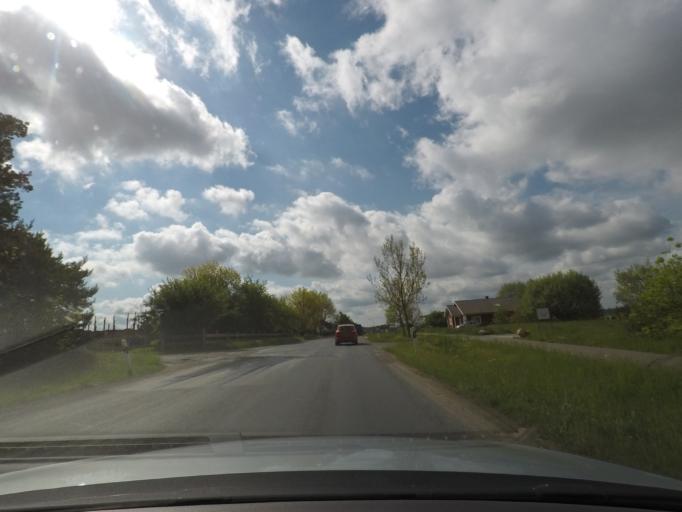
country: DE
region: Lower Saxony
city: Helmstedt
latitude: 52.2460
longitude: 10.9970
